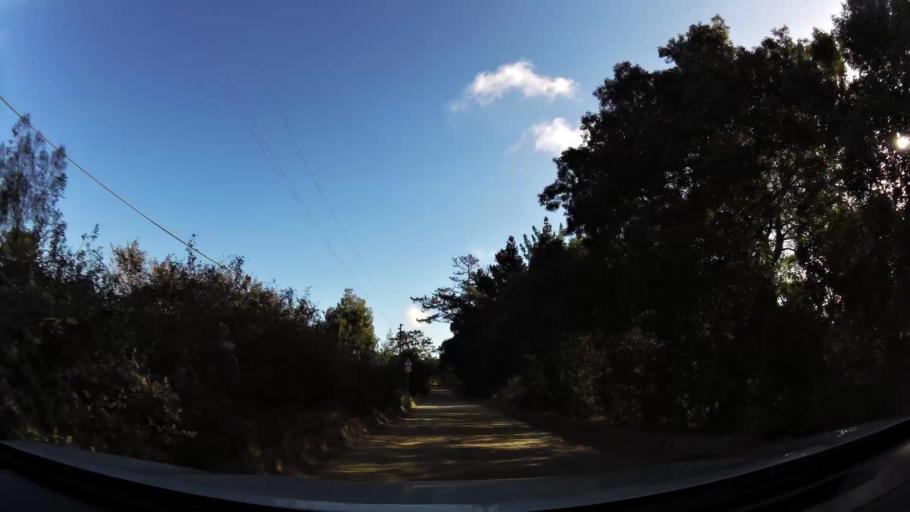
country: ZA
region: Western Cape
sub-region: Eden District Municipality
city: George
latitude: -33.9805
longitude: 22.5710
